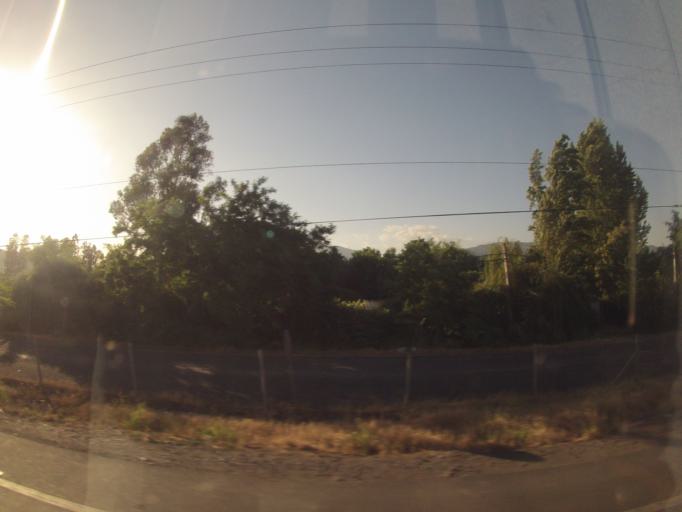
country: CL
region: O'Higgins
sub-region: Provincia de Colchagua
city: Chimbarongo
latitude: -34.6083
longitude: -70.9853
